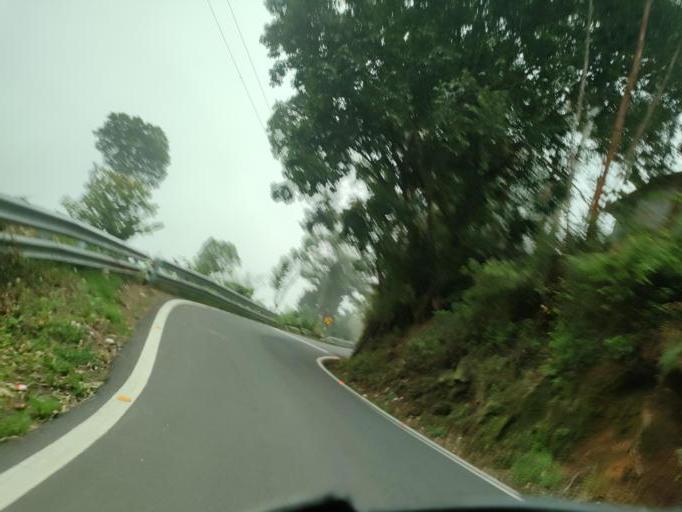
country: IN
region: Tamil Nadu
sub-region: Dindigul
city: Ayakudi
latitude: 10.3334
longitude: 77.5624
